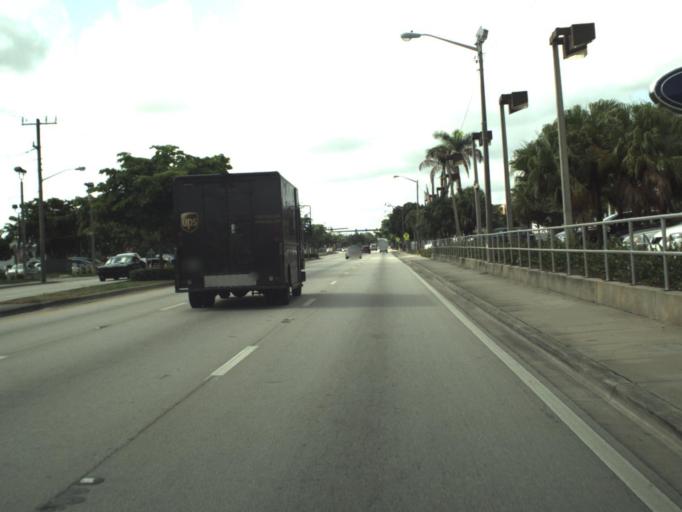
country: US
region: Florida
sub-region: Broward County
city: Broward Estates
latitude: 26.1309
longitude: -80.2024
